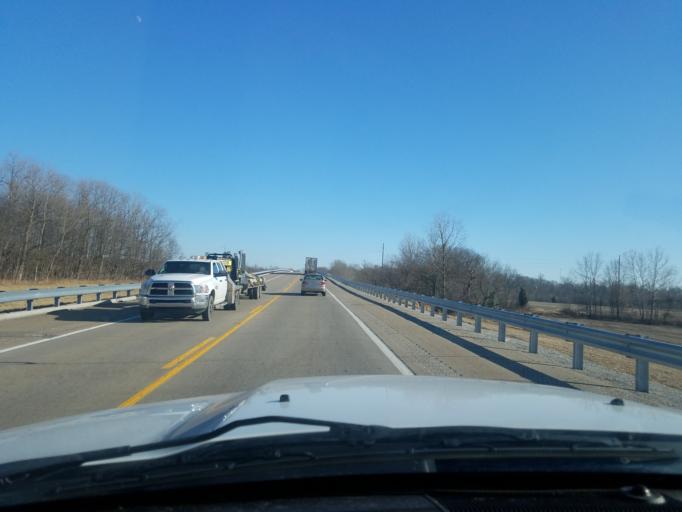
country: US
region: Kentucky
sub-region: Henderson County
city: Henderson
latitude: 37.7906
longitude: -87.6385
